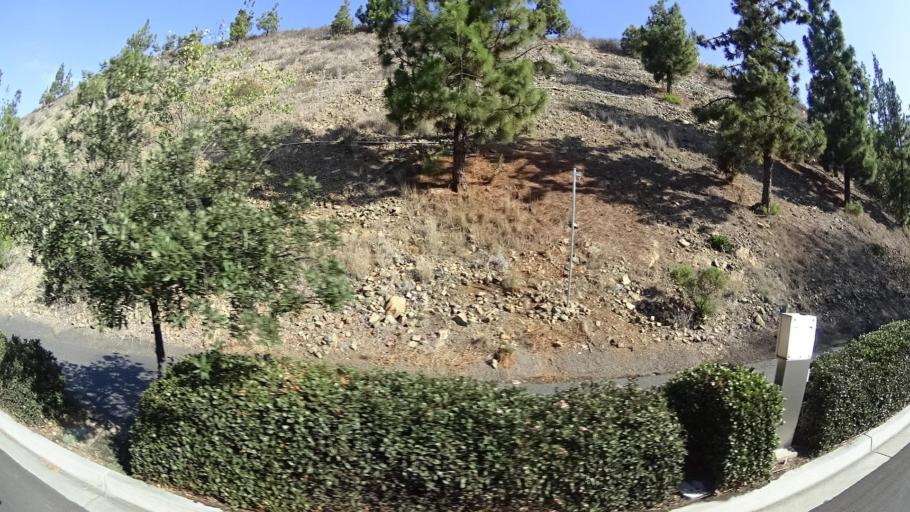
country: US
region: California
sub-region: San Diego County
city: Lake San Marcos
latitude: 33.1021
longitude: -117.1907
